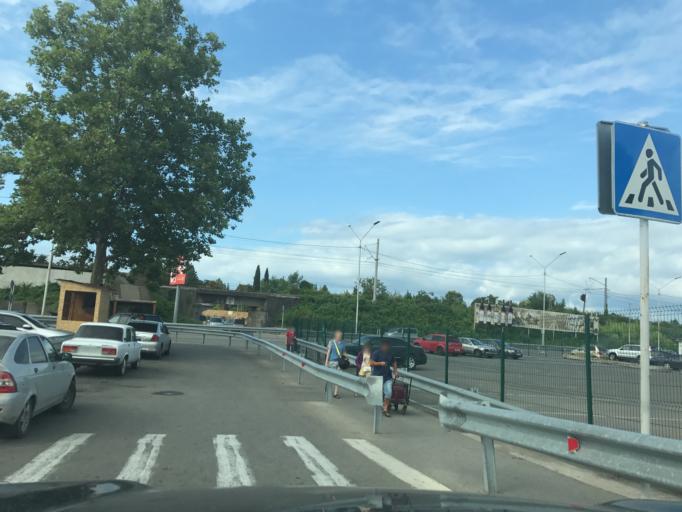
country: GE
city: Gantiadi
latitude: 43.3938
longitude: 40.0129
